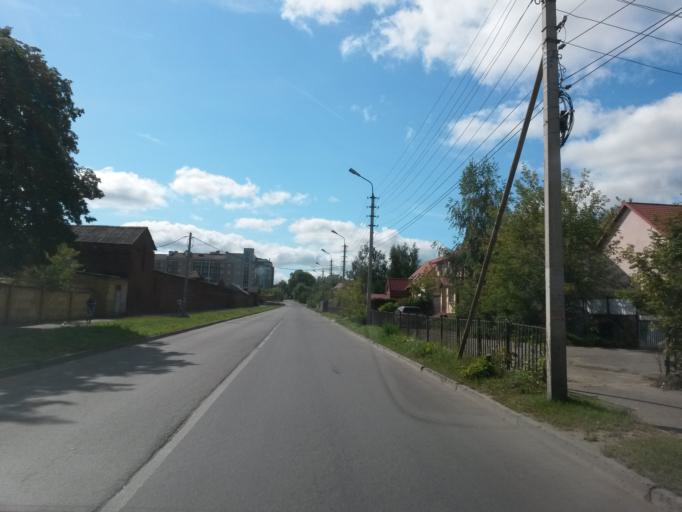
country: RU
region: Jaroslavl
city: Yaroslavl
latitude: 57.6081
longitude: 39.8732
